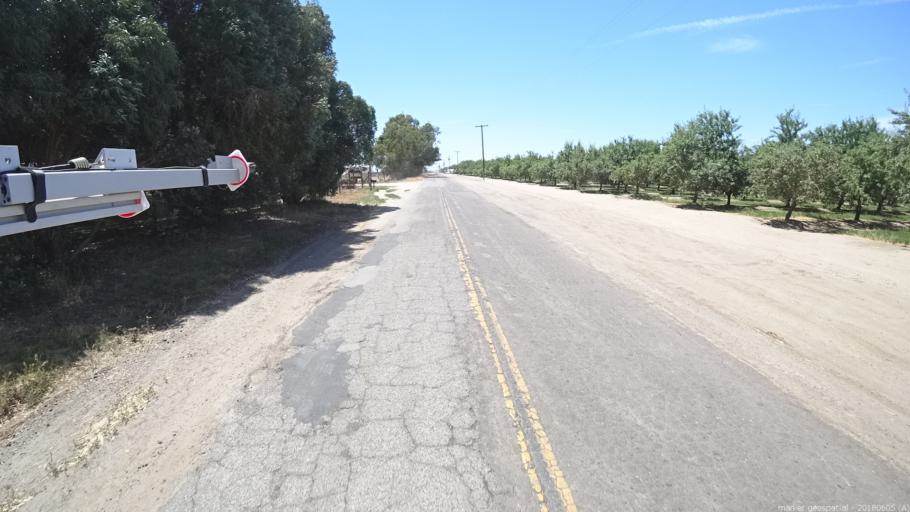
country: US
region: California
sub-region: Madera County
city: Chowchilla
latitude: 37.1123
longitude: -120.3652
